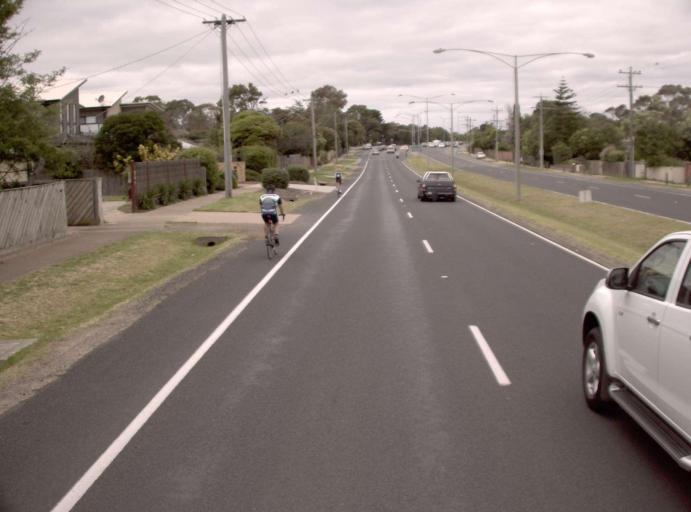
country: AU
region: Victoria
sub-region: Mornington Peninsula
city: Mornington
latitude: -38.2420
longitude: 145.0369
